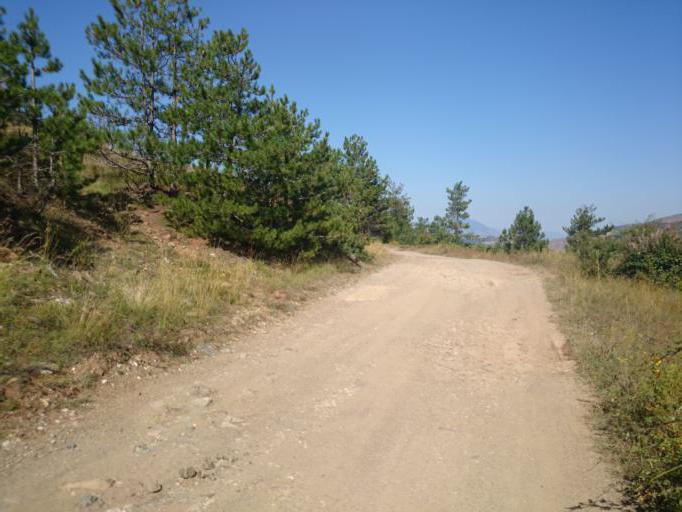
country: AL
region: Diber
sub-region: Rrethi i Bulqizes
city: Martanesh
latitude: 41.3981
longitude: 20.2624
